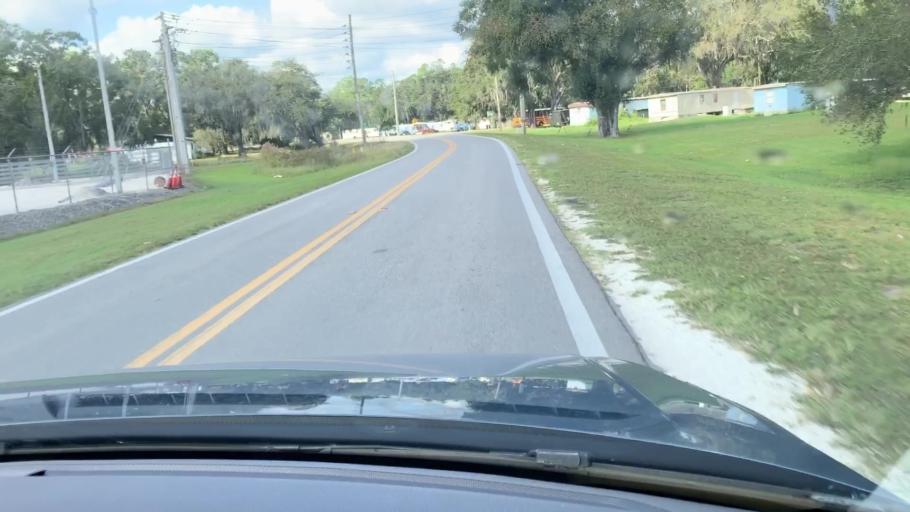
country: US
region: Florida
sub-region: Polk County
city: Winston
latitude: 28.0323
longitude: -81.9994
